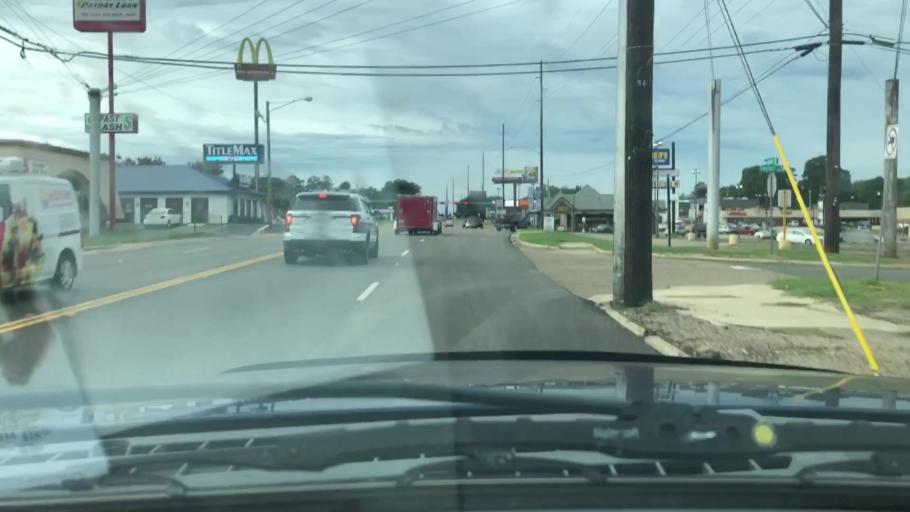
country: US
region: Texas
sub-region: Bowie County
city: Texarkana
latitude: 33.4351
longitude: -94.0607
